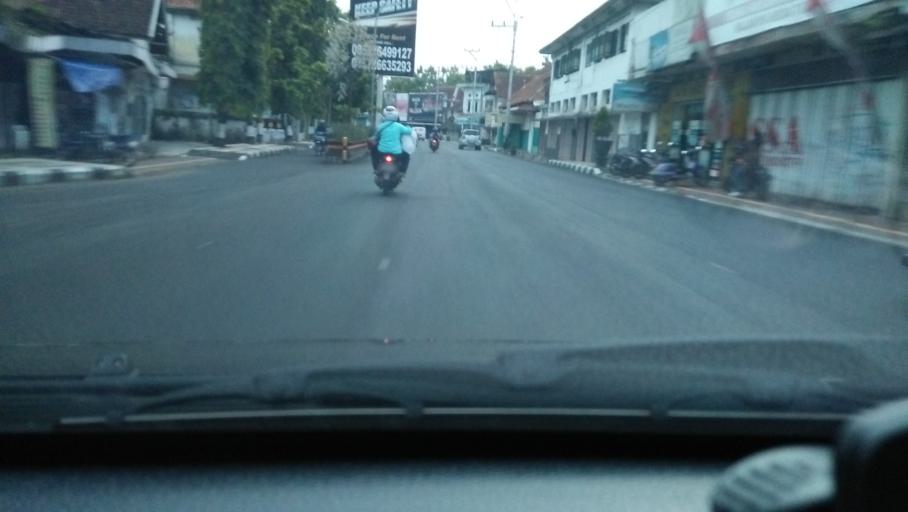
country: ID
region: Central Java
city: Magelang
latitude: -7.4691
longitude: 110.2187
